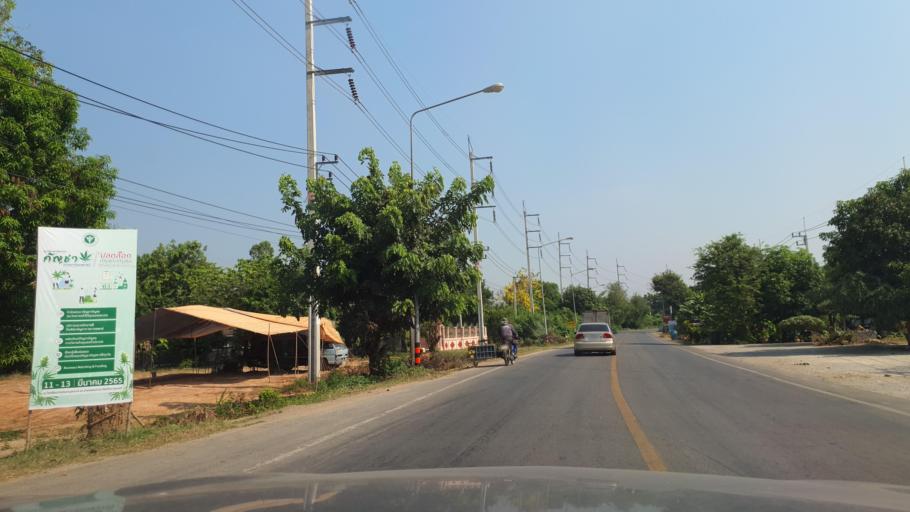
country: TH
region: Kanchanaburi
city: Kanchanaburi
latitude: 14.0454
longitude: 99.4716
